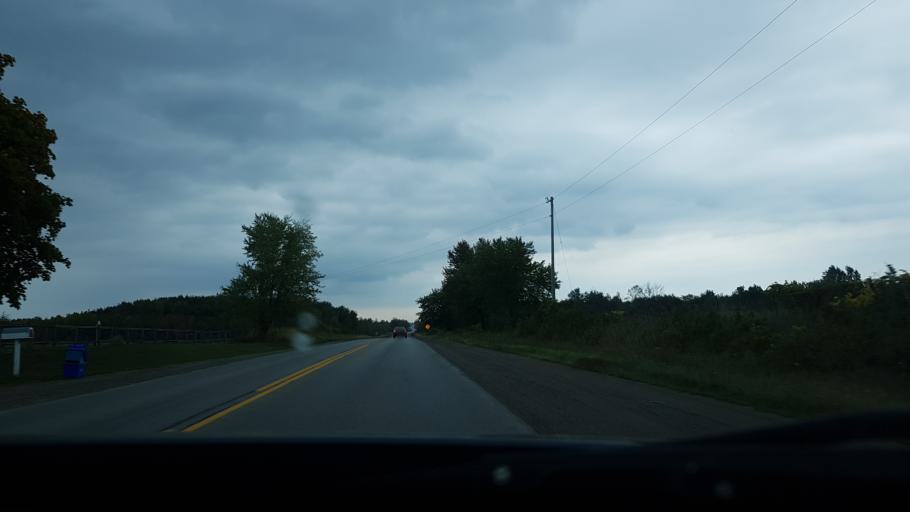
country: CA
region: Ontario
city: Omemee
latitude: 44.3673
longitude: -78.6845
